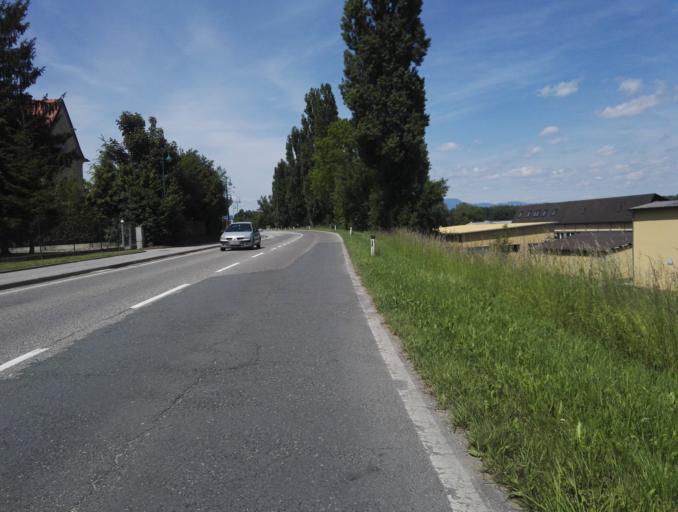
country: AT
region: Styria
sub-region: Politischer Bezirk Graz-Umgebung
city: Kalsdorf bei Graz
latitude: 46.9668
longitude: 15.4761
